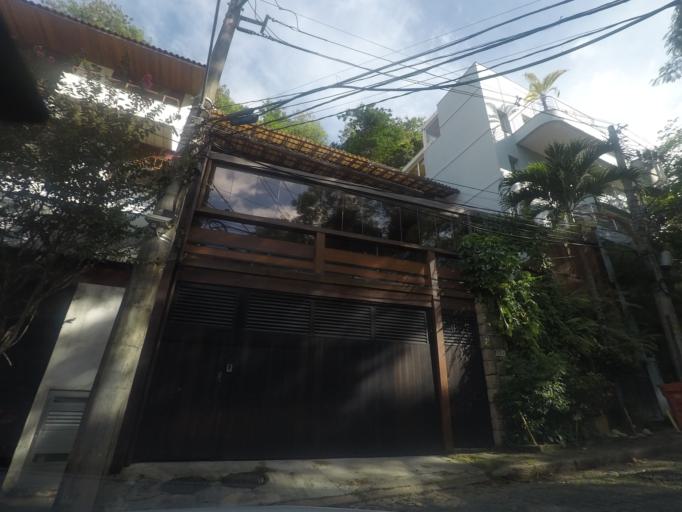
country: BR
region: Rio de Janeiro
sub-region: Rio De Janeiro
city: Rio de Janeiro
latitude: -22.9602
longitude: -43.2001
